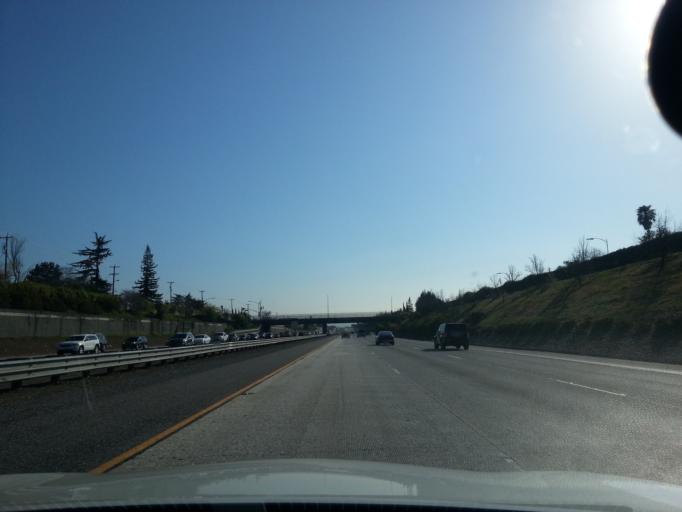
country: US
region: California
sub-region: Santa Clara County
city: Cambrian Park
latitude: 37.2504
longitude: -121.9253
